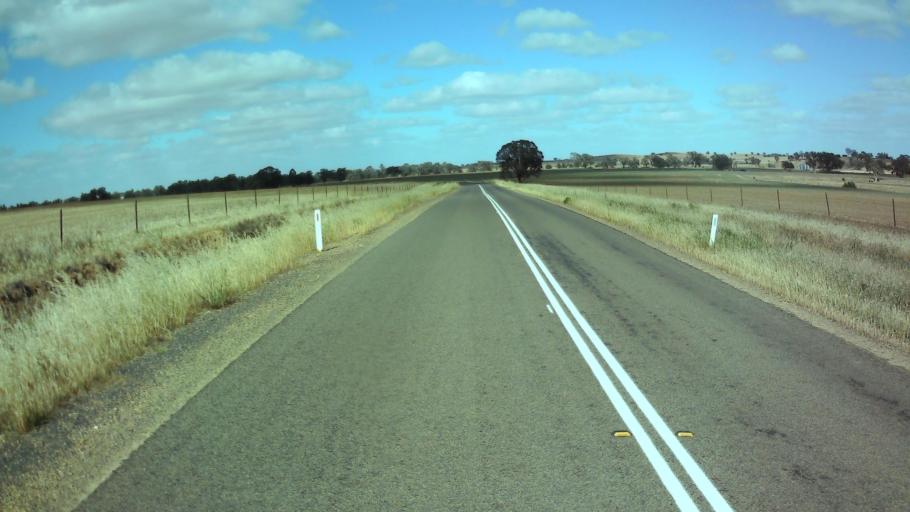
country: AU
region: New South Wales
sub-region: Weddin
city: Grenfell
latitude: -33.9775
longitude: 148.4230
